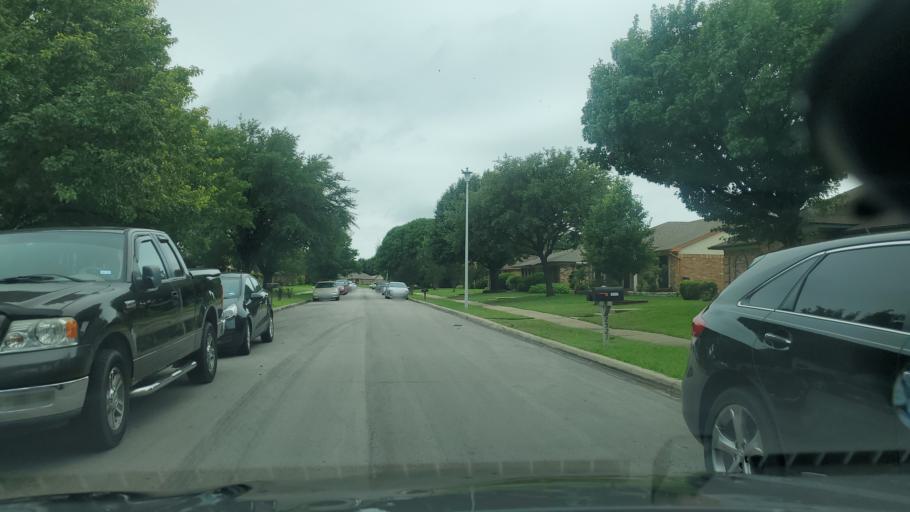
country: US
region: Texas
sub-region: Dallas County
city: Garland
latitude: 32.9426
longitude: -96.6286
